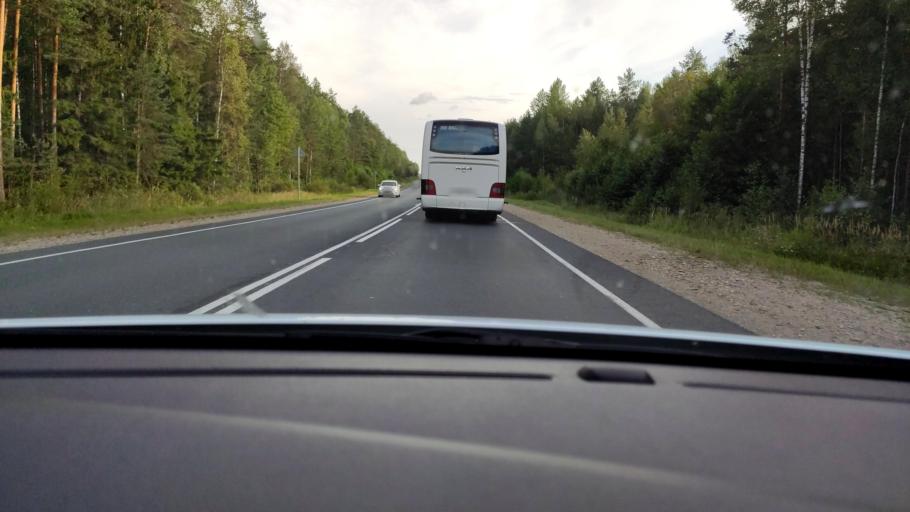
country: RU
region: Mariy-El
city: Suslonger
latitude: 56.2948
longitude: 48.2335
